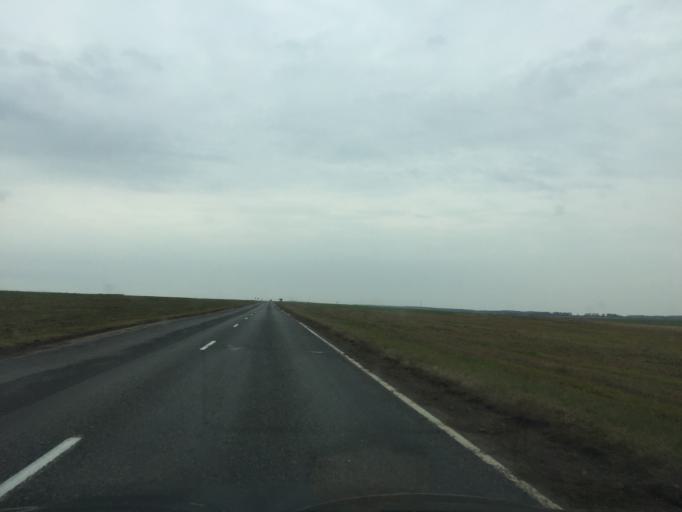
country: BY
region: Gomel
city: Dowsk
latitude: 53.1827
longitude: 30.4984
